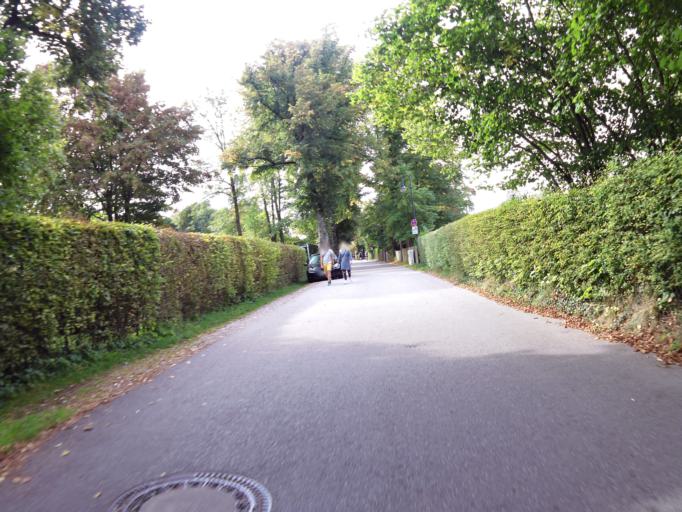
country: DE
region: Bavaria
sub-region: Upper Bavaria
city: Berg
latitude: 47.9742
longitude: 11.3529
